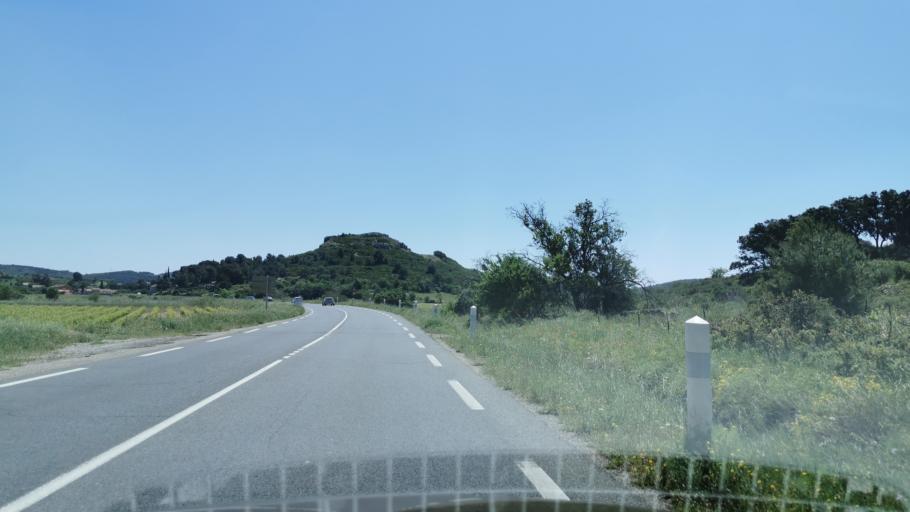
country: FR
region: Languedoc-Roussillon
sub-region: Departement de l'Aude
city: Nevian
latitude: 43.1856
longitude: 2.9198
